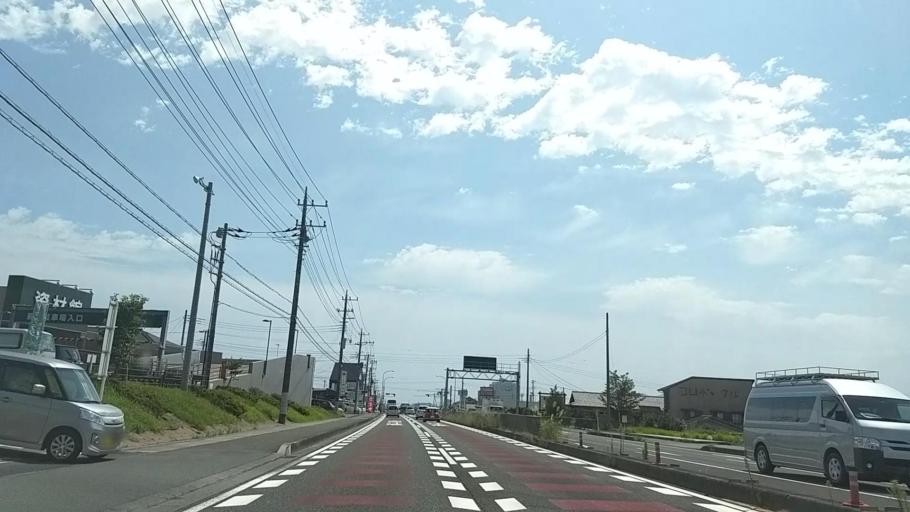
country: JP
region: Shizuoka
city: Fujinomiya
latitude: 35.2553
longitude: 138.6157
